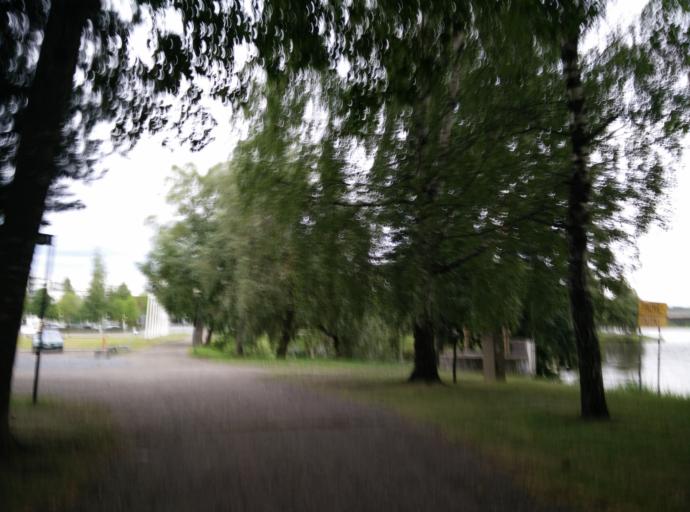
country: FI
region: Haeme
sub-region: Haemeenlinna
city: Haemeenlinna
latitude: 60.9972
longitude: 24.4750
